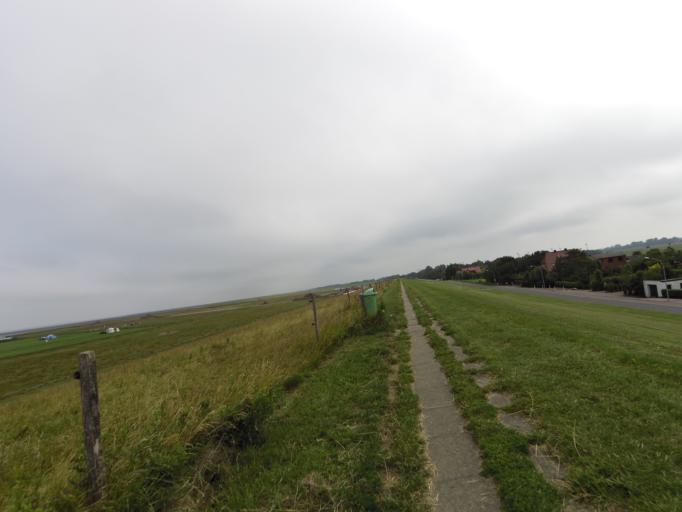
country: DE
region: Lower Saxony
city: Padingbuttel
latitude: 53.7391
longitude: 8.5191
